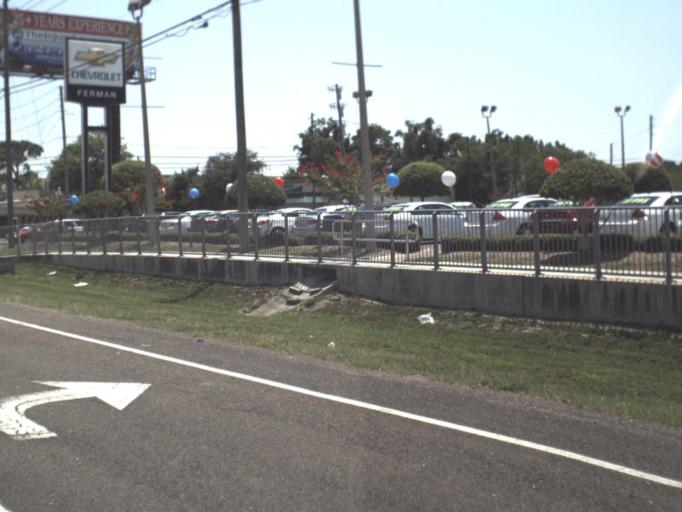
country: US
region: Florida
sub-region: Pasco County
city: Holiday
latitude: 28.1674
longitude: -82.7406
